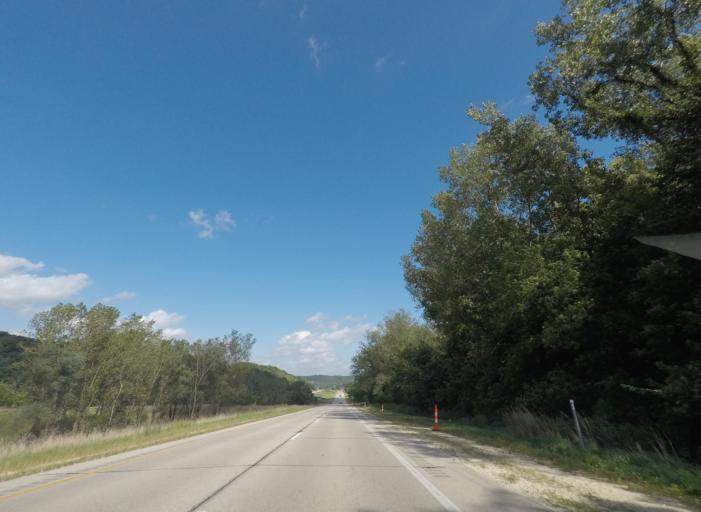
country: US
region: Iowa
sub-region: Dubuque County
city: Dubuque
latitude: 42.4177
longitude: -90.7161
